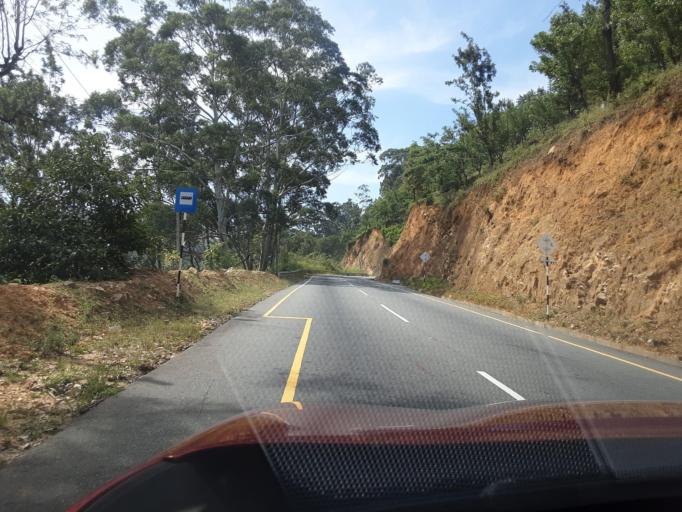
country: LK
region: Uva
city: Badulla
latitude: 6.9618
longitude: 81.1109
